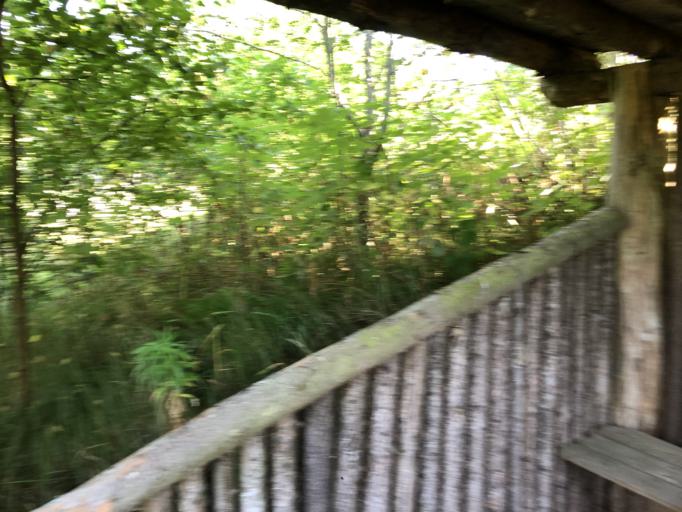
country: DK
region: Central Jutland
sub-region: Holstebro Kommune
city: Ulfborg
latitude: 56.3269
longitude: 8.4152
